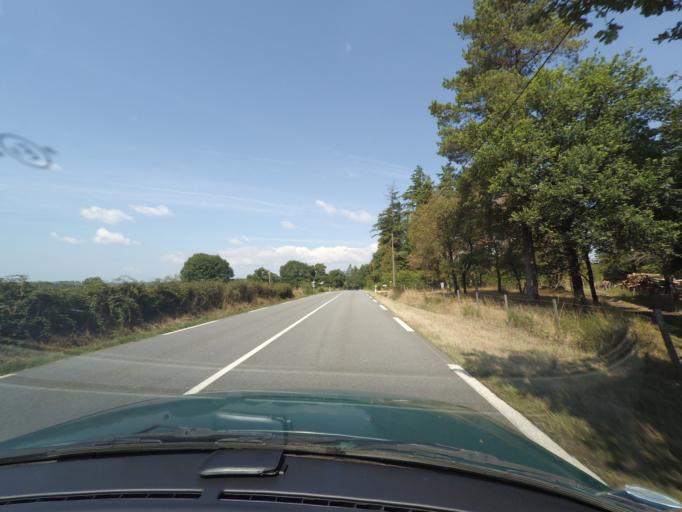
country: FR
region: Limousin
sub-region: Departement de la Haute-Vienne
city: Feytiat
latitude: 45.8033
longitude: 1.3748
